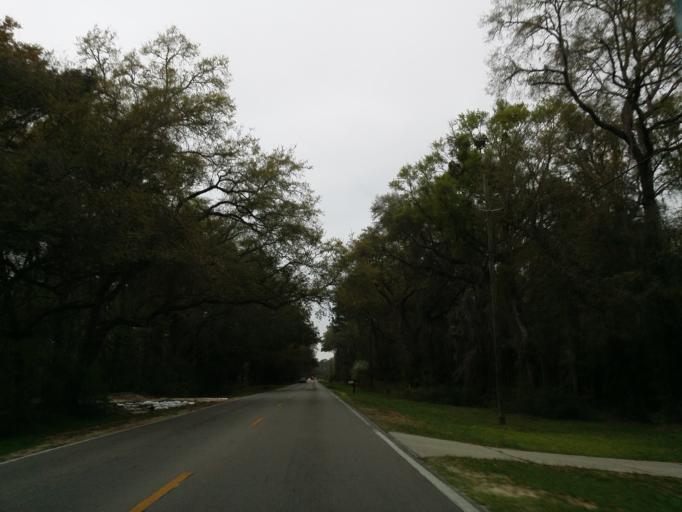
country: US
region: Florida
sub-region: Leon County
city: Woodville
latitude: 30.3242
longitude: -84.3057
